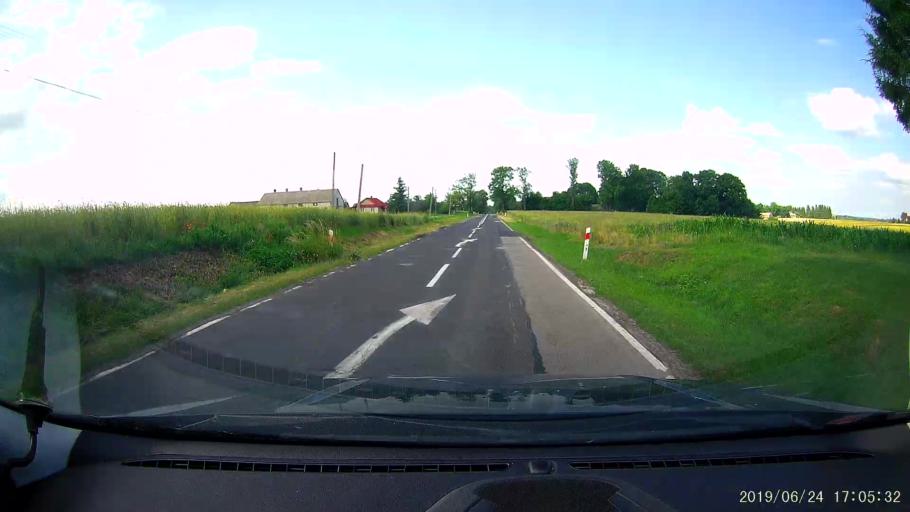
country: PL
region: Lublin Voivodeship
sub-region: Powiat hrubieszowski
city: Dolhobyczow
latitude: 50.5764
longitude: 23.9653
